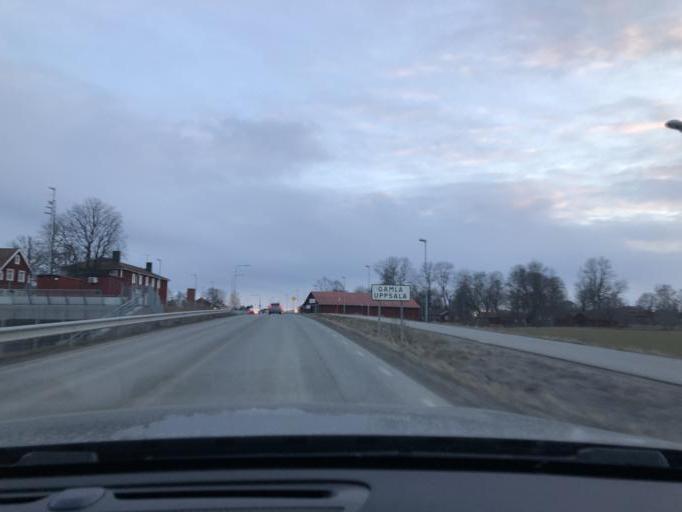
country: SE
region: Uppsala
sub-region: Uppsala Kommun
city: Gamla Uppsala
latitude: 59.9002
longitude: 17.6389
